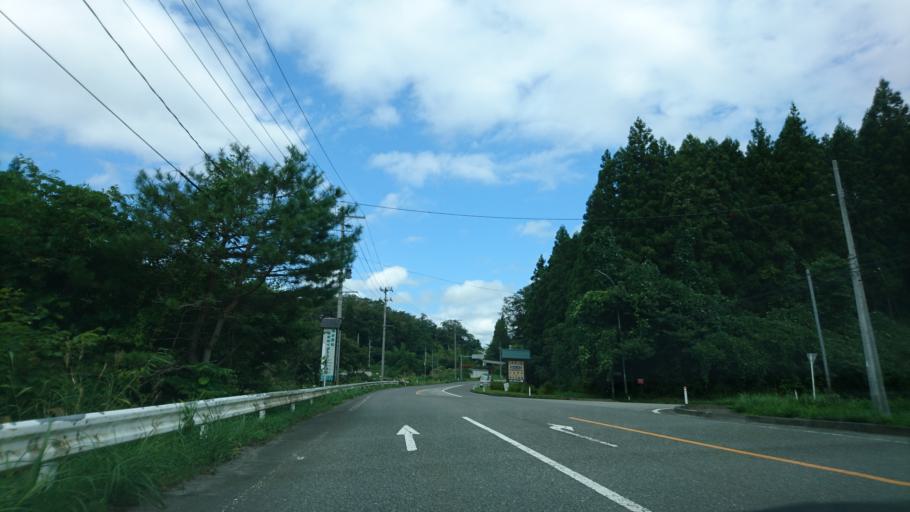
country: JP
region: Miyagi
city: Furukawa
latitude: 38.7731
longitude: 140.8632
